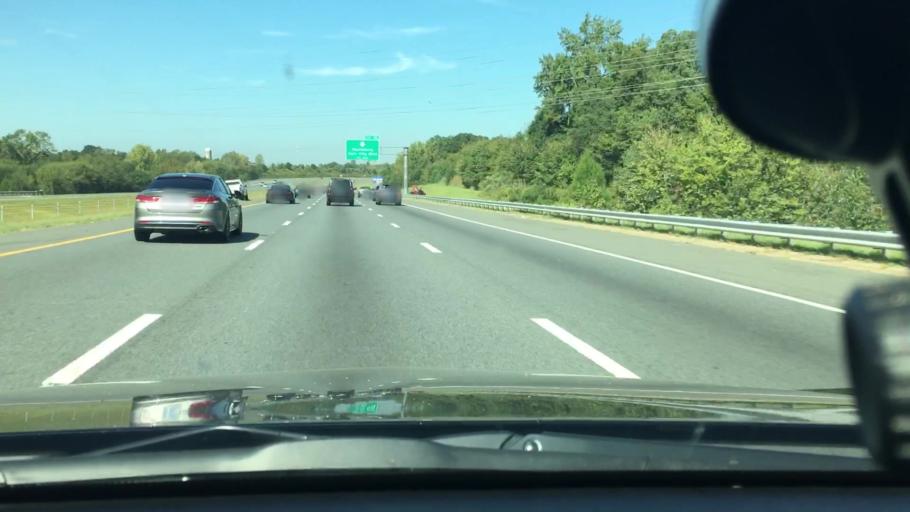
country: US
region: North Carolina
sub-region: Cabarrus County
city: Harrisburg
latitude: 35.3079
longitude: -80.6982
